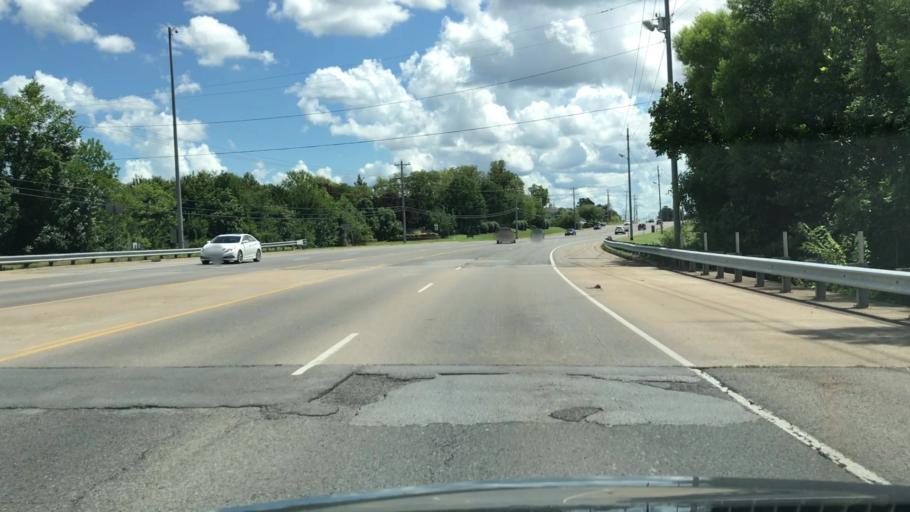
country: US
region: Tennessee
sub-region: Rutherford County
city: Murfreesboro
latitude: 35.8447
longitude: -86.4603
